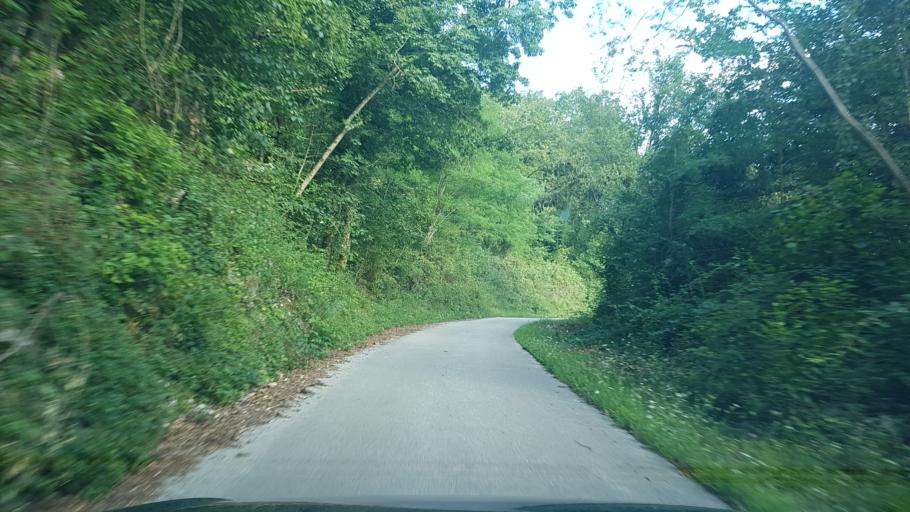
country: SI
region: Kanal
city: Deskle
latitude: 46.0284
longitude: 13.6089
